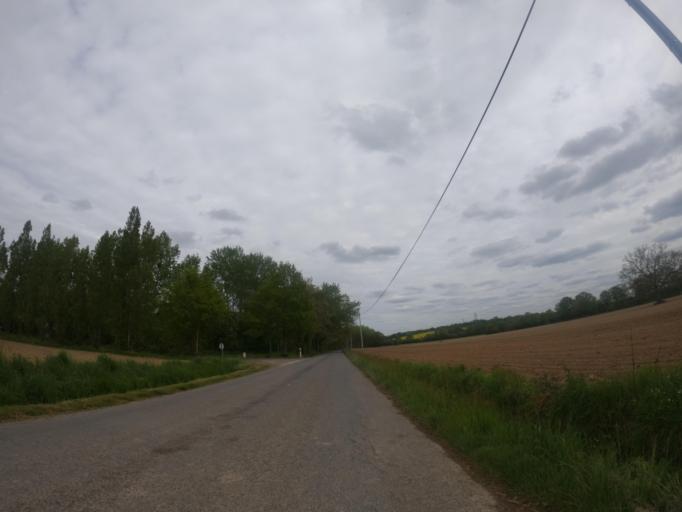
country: FR
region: Pays de la Loire
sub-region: Departement de la Loire-Atlantique
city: Rouge
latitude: 47.7379
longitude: -1.4354
